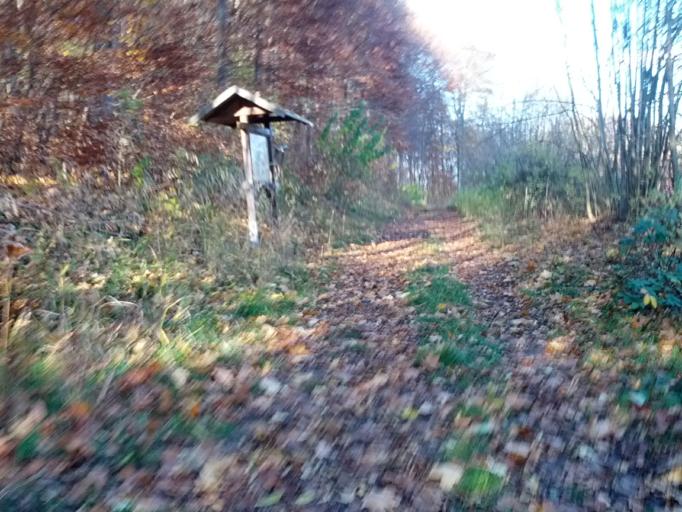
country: DE
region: Thuringia
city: Thal
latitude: 50.9138
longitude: 10.3992
